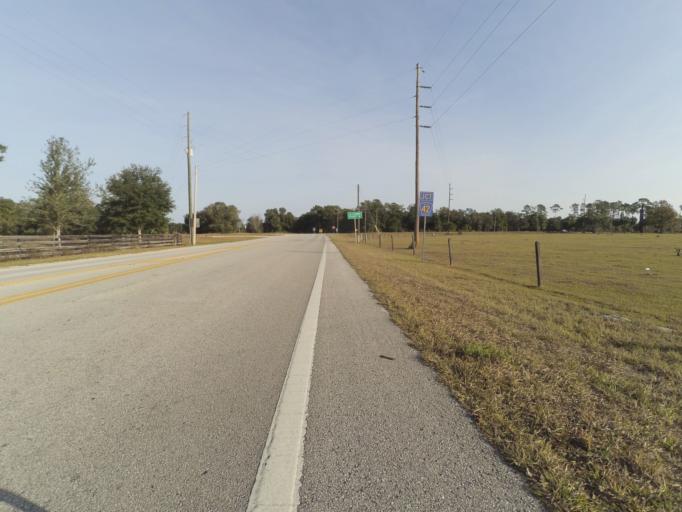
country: US
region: Florida
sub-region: Lake County
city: Umatilla
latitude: 28.9595
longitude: -81.6276
